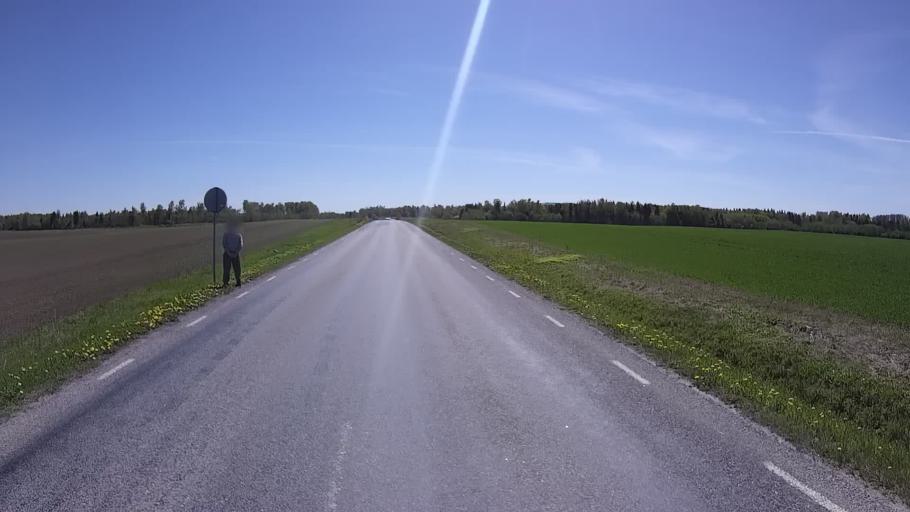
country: EE
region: Harju
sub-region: Raasiku vald
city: Raasiku
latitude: 59.0995
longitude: 25.1698
